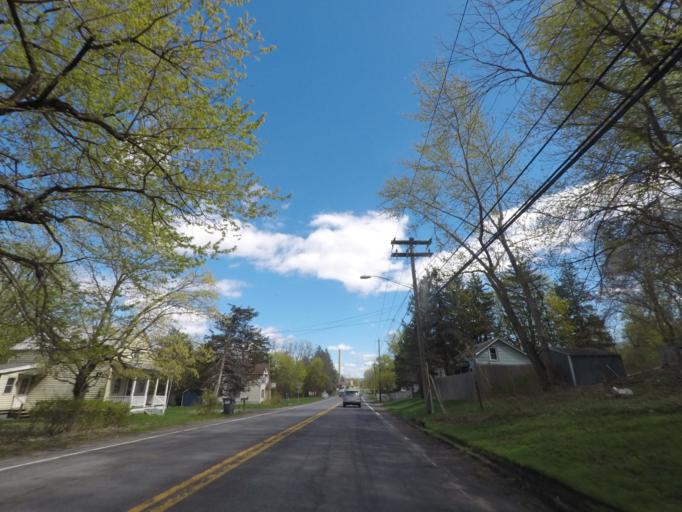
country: US
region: New York
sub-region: Columbia County
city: Oakdale
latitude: 42.2424
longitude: -73.7659
